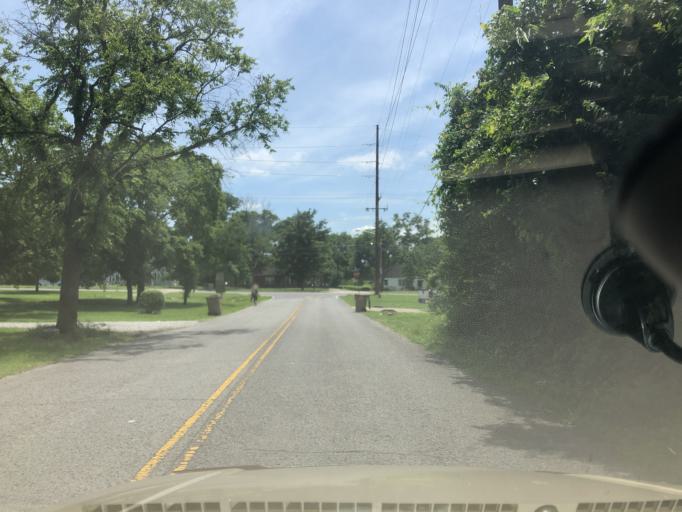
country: US
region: Tennessee
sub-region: Davidson County
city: Goodlettsville
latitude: 36.2562
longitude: -86.7043
